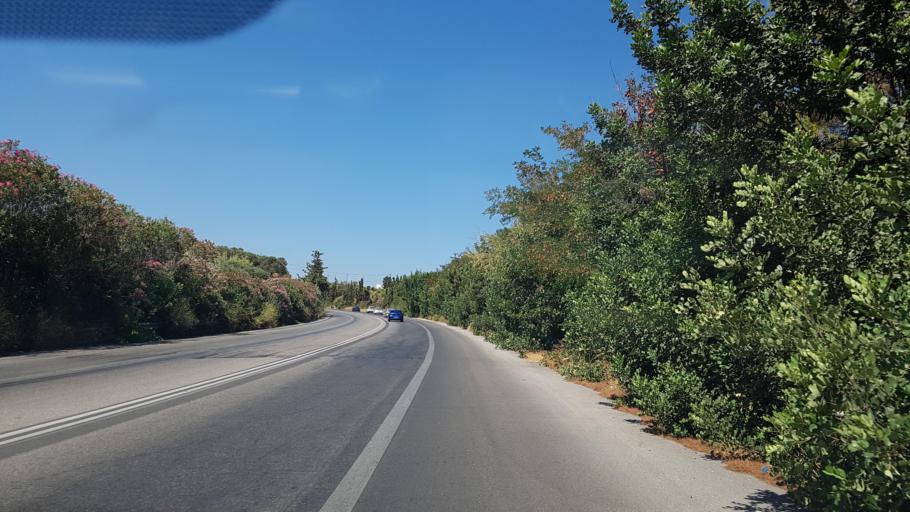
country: GR
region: Crete
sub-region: Nomos Chanias
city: Gerani
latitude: 35.5163
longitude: 23.8618
